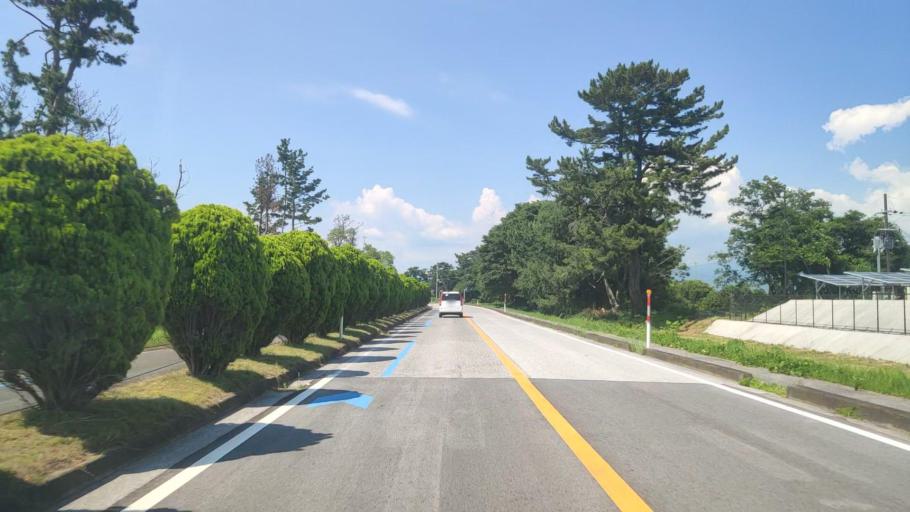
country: JP
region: Shiga Prefecture
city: Nagahama
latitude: 35.3951
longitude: 136.2179
